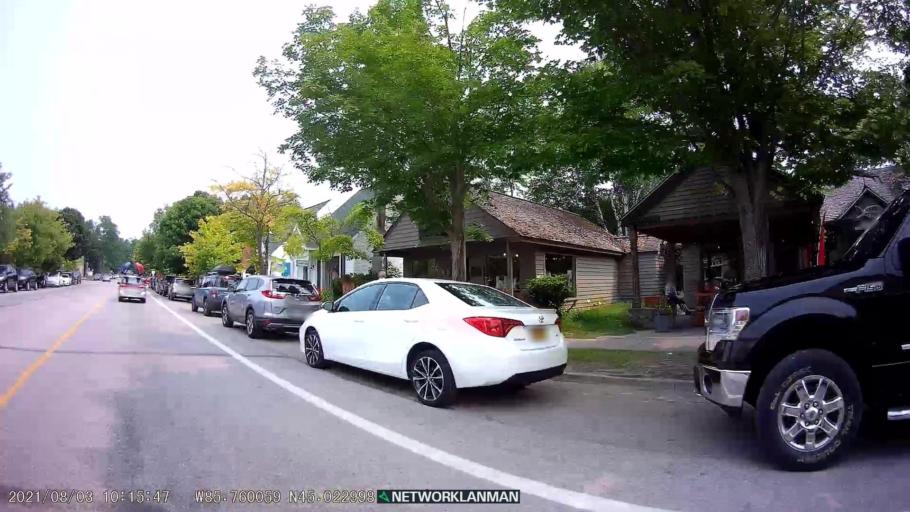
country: US
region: Michigan
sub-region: Leelanau County
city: Leland
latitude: 45.0250
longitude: -85.7590
